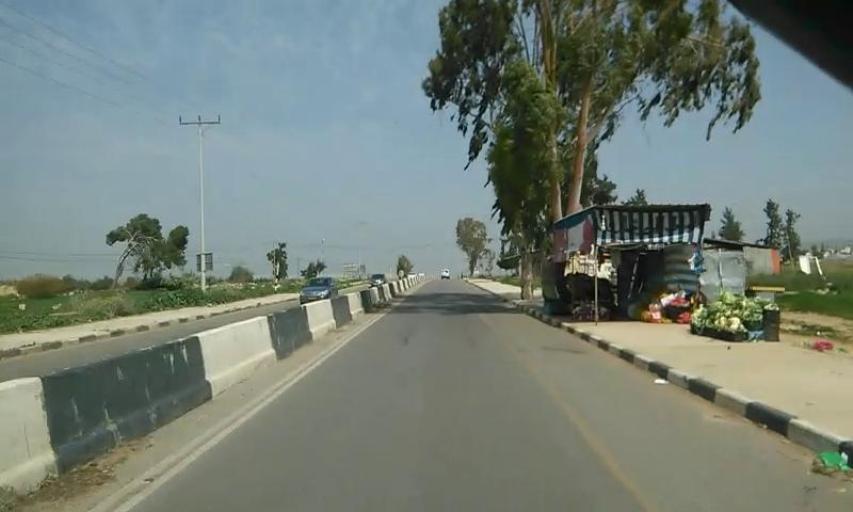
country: PS
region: West Bank
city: Al Jalamah
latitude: 32.5060
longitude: 35.3047
